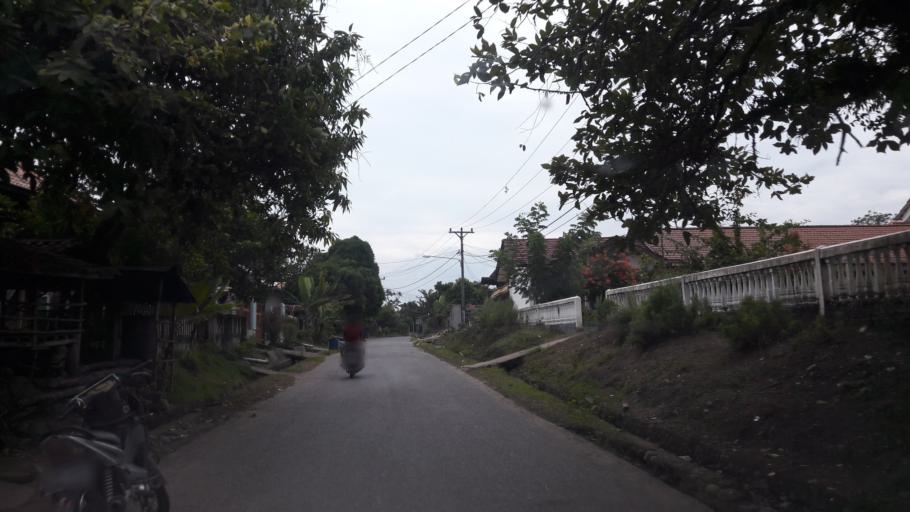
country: ID
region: South Sumatra
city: Gunungmenang
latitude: -3.1480
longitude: 104.1154
